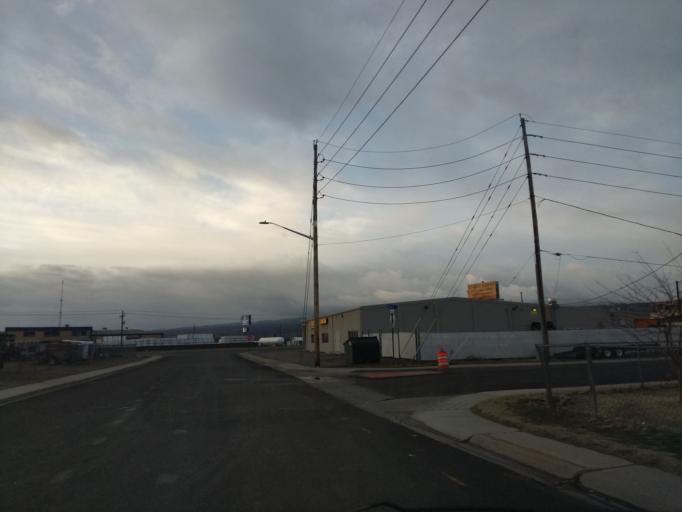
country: US
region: Colorado
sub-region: Mesa County
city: Grand Junction
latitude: 39.0685
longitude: -108.5407
